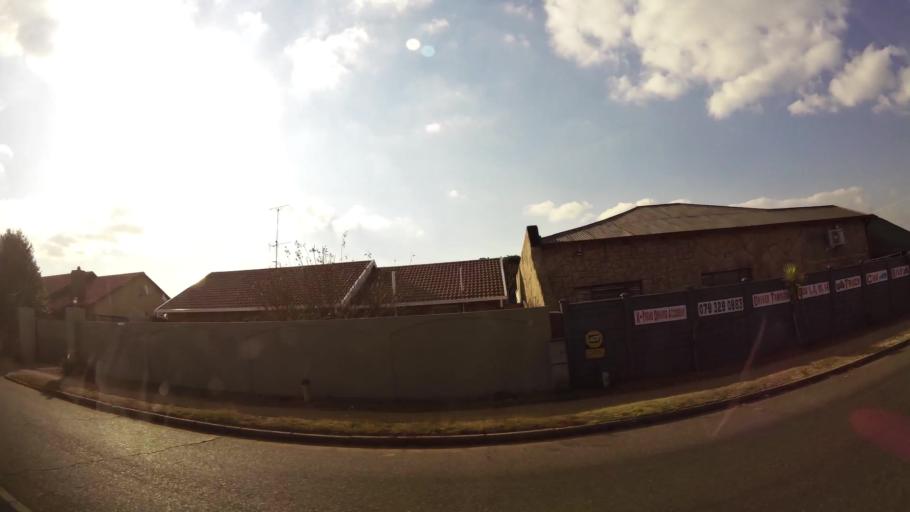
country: ZA
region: Gauteng
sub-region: West Rand District Municipality
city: Krugersdorp
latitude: -26.0931
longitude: 27.7475
